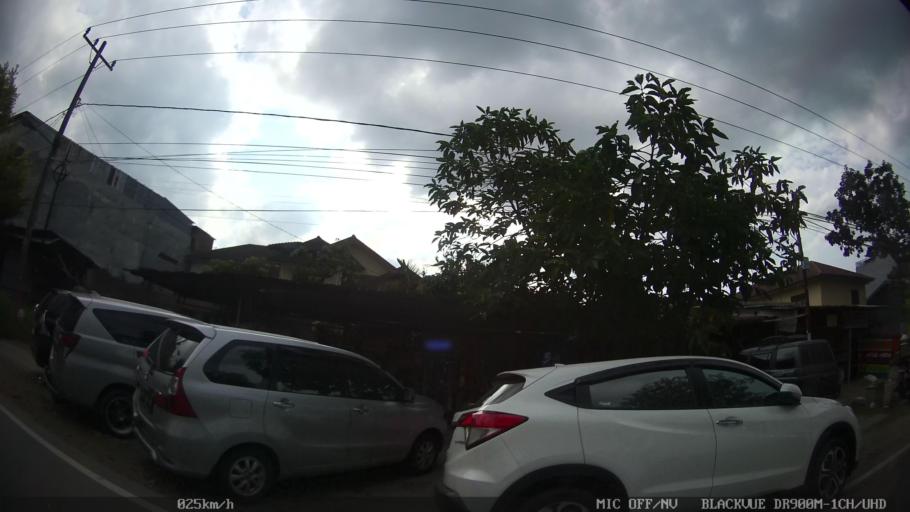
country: ID
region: North Sumatra
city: Sunggal
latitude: 3.5426
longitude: 98.6045
